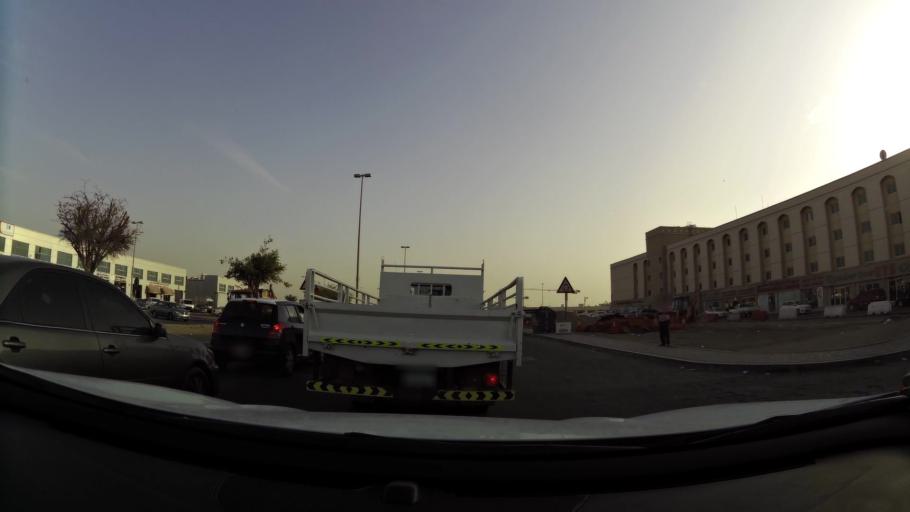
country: AE
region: Abu Dhabi
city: Abu Dhabi
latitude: 24.3478
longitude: 54.5121
